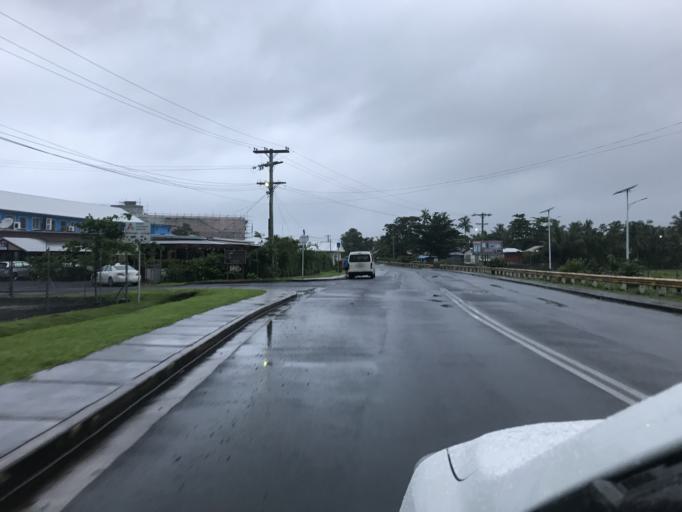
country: WS
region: Tuamasaga
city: Apia
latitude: -13.8330
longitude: -171.7665
